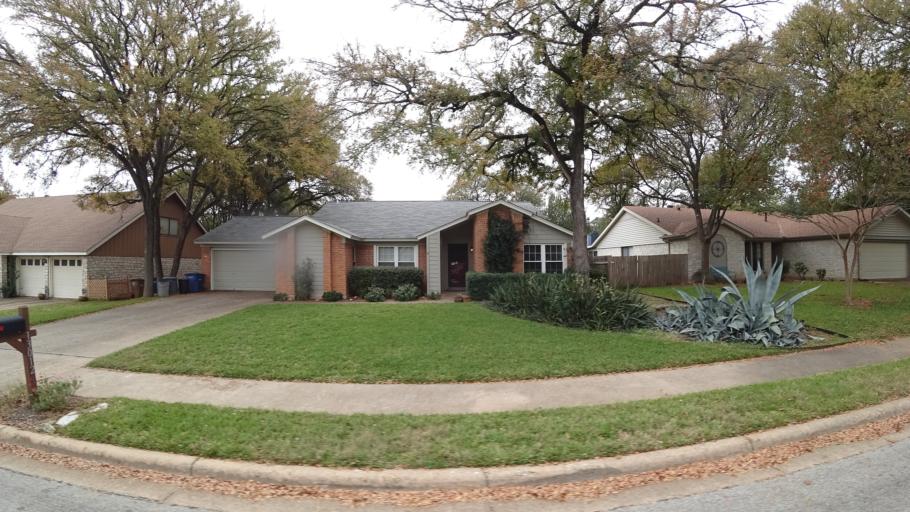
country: US
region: Texas
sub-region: Travis County
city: Wells Branch
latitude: 30.4309
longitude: -97.7127
